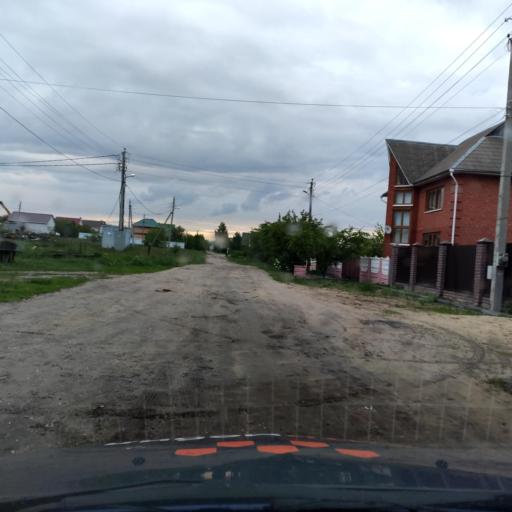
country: RU
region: Voronezj
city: Maslovka
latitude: 51.5435
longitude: 39.2393
